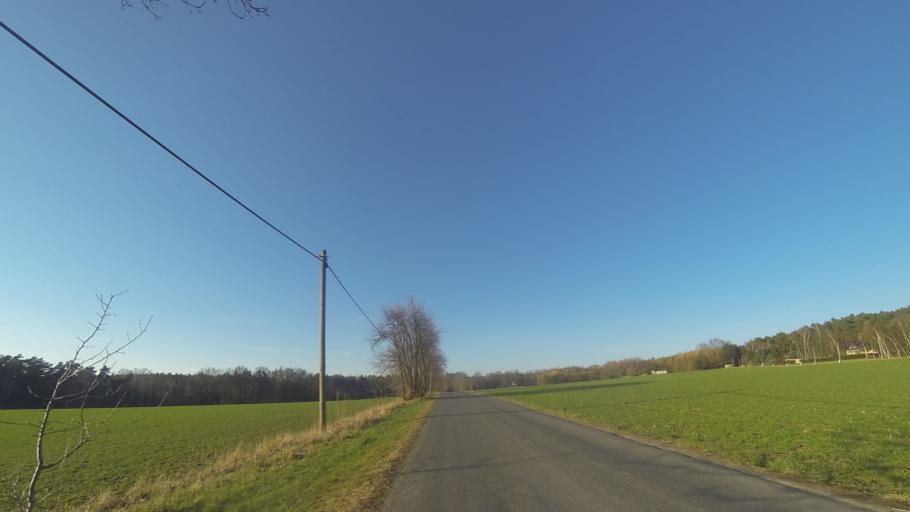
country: DE
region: Saxony
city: Ottendorf-Okrilla
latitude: 51.1905
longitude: 13.7948
